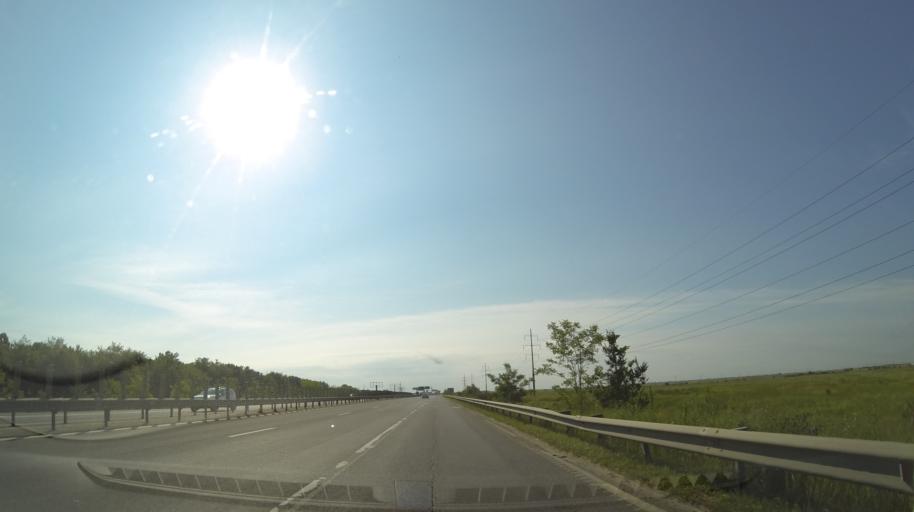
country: RO
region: Arges
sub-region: Oras Stefanesti
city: Golesti
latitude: 44.8118
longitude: 24.9560
